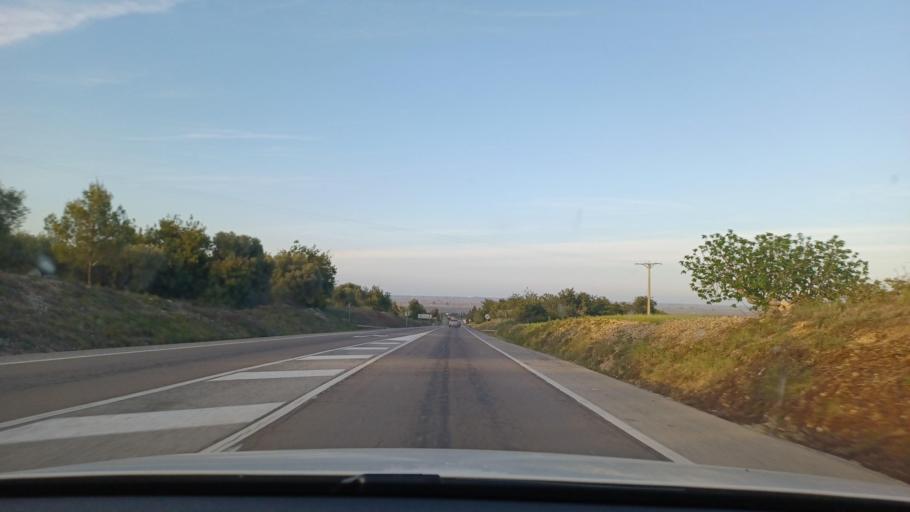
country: ES
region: Catalonia
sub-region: Provincia de Tarragona
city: Sant Carles de la Rapita
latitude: 40.6312
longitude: 0.5830
